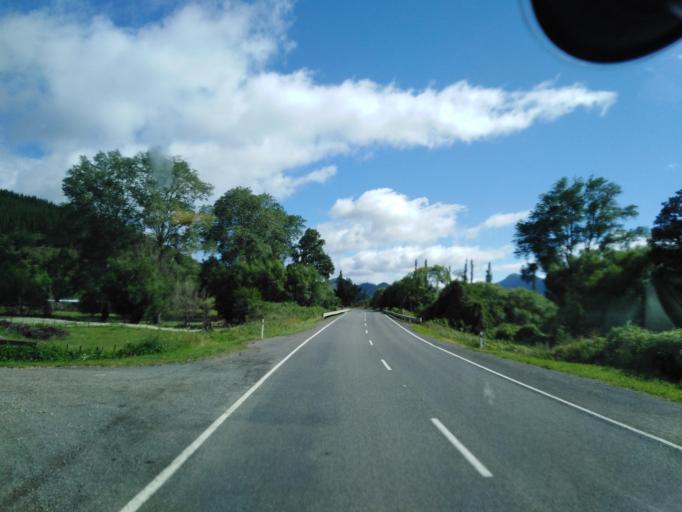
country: NZ
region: Nelson
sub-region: Nelson City
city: Nelson
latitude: -41.2504
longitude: 173.5775
